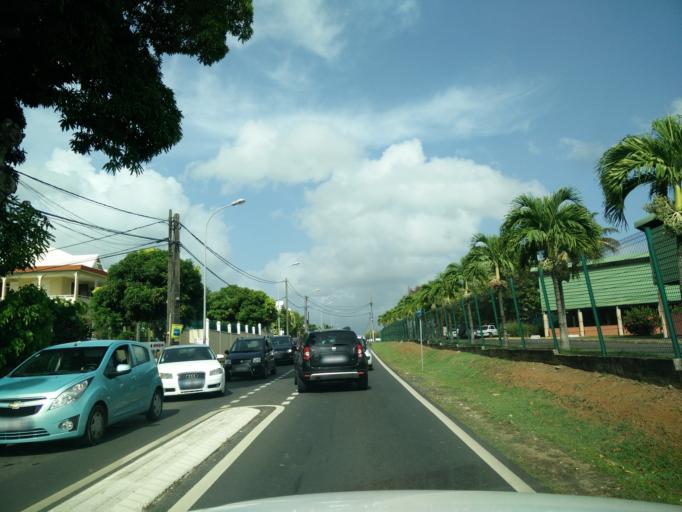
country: GP
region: Guadeloupe
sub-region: Guadeloupe
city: Baie-Mahault
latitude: 16.2411
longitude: -61.5926
